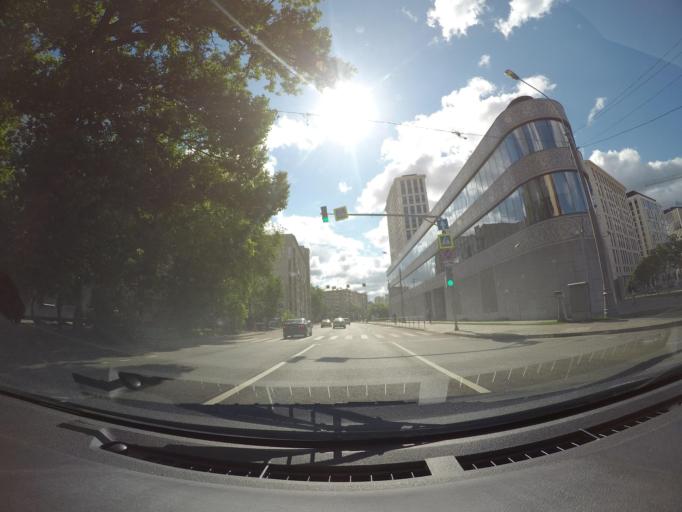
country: RU
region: Moskovskaya
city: Dorogomilovo
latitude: 55.7916
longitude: 37.5662
